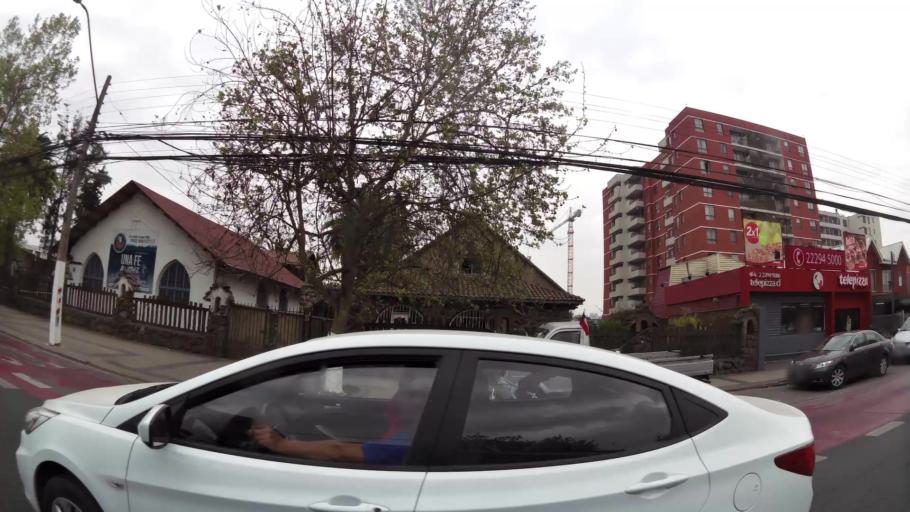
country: CL
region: Santiago Metropolitan
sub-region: Provincia de Santiago
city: Villa Presidente Frei, Nunoa, Santiago, Chile
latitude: -33.4847
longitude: -70.5993
